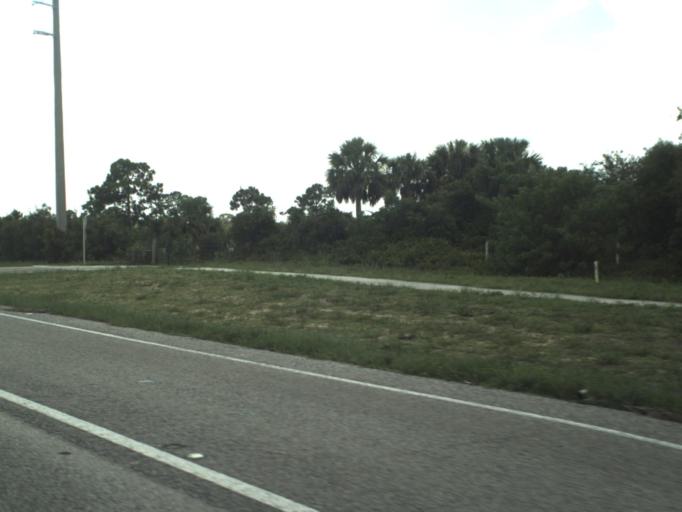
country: US
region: Florida
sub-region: Martin County
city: Hobe Sound
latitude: 27.0972
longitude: -80.1581
